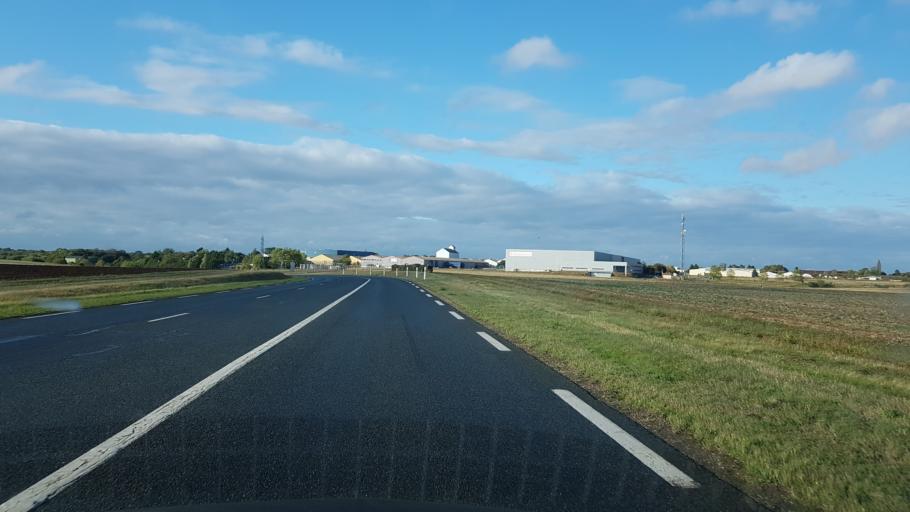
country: FR
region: Centre
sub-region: Departement du Loiret
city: Sermaises
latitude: 48.2848
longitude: 2.2072
